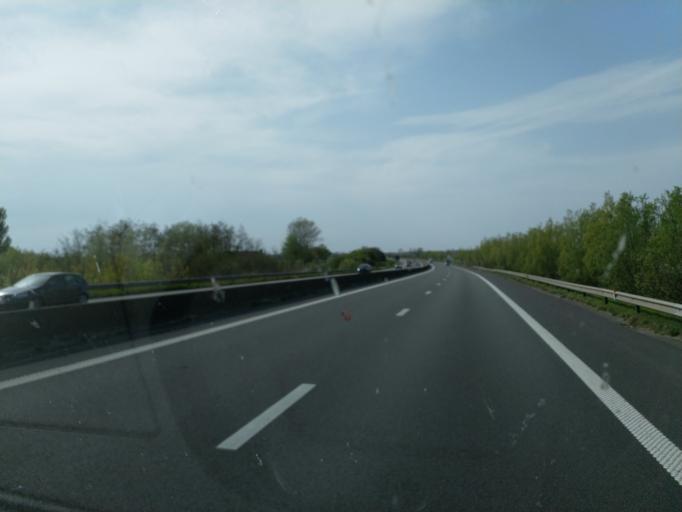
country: BE
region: Flanders
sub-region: Provincie West-Vlaanderen
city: Veurne
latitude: 51.0607
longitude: 2.6452
